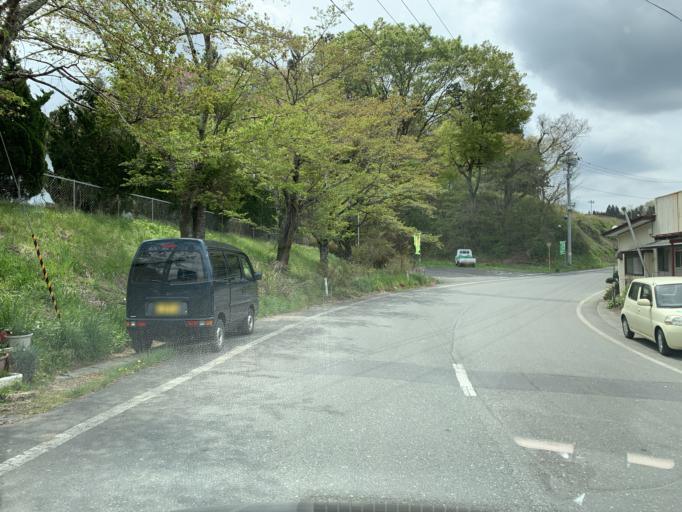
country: JP
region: Iwate
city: Ichinoseki
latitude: 38.8566
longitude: 141.3339
